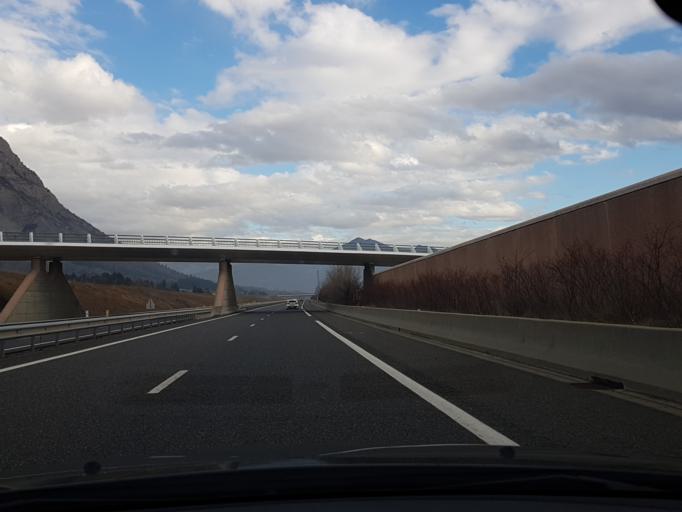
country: FR
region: Provence-Alpes-Cote d'Azur
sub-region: Departement des Hautes-Alpes
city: Laragne-Monteglin
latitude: 44.3863
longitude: 5.9369
